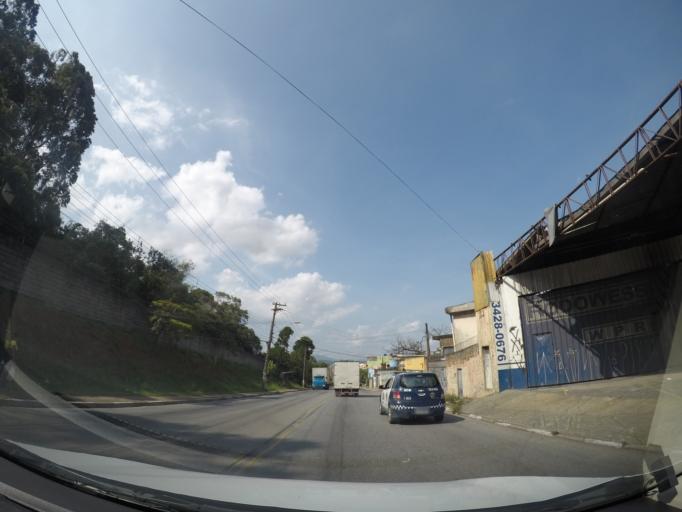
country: BR
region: Sao Paulo
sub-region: Guarulhos
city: Guarulhos
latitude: -23.4450
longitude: -46.4707
